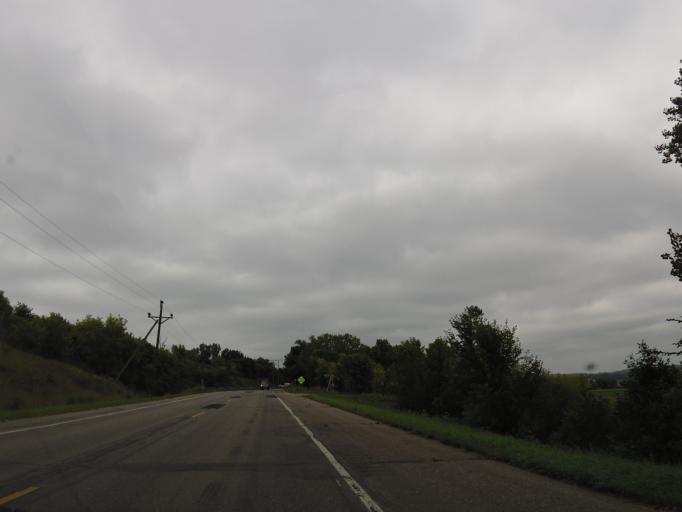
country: US
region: Minnesota
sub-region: Yellow Medicine County
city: Granite Falls
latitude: 44.8258
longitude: -95.5980
